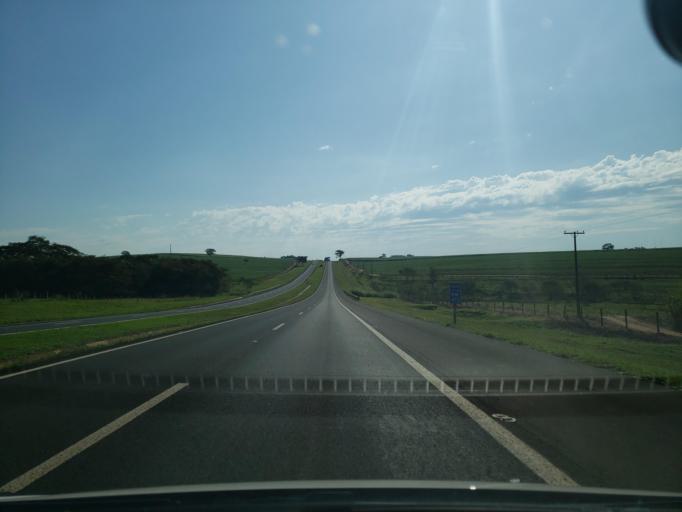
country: BR
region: Sao Paulo
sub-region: Promissao
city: Promissao
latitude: -21.5291
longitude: -49.9874
